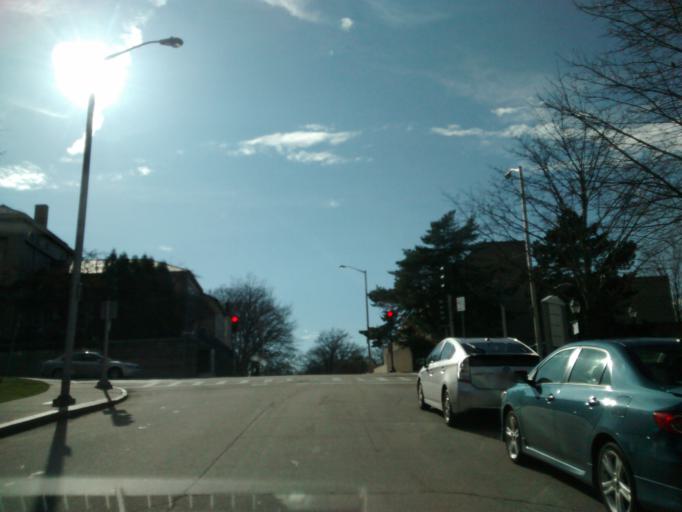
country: US
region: Massachusetts
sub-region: Worcester County
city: Worcester
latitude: 42.2723
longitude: -71.8011
